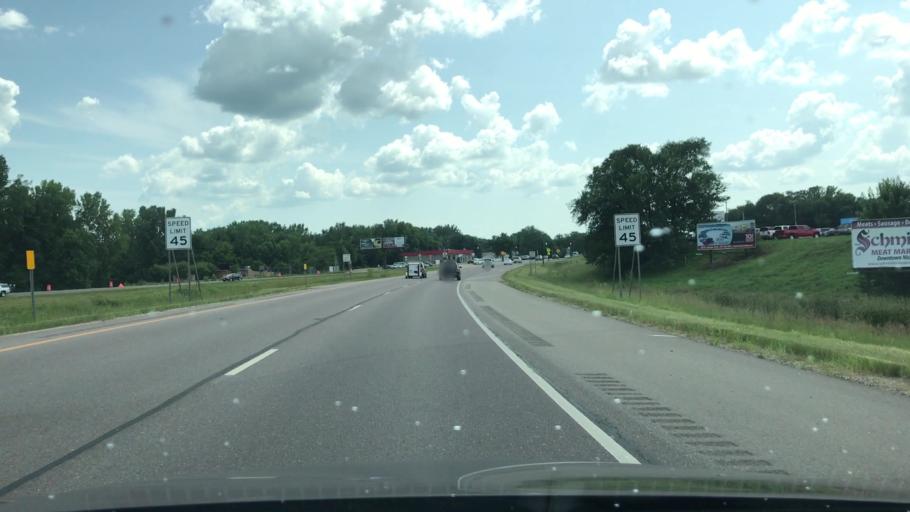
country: US
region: Minnesota
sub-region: Nicollet County
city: Saint Peter
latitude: 44.3357
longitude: -93.9483
